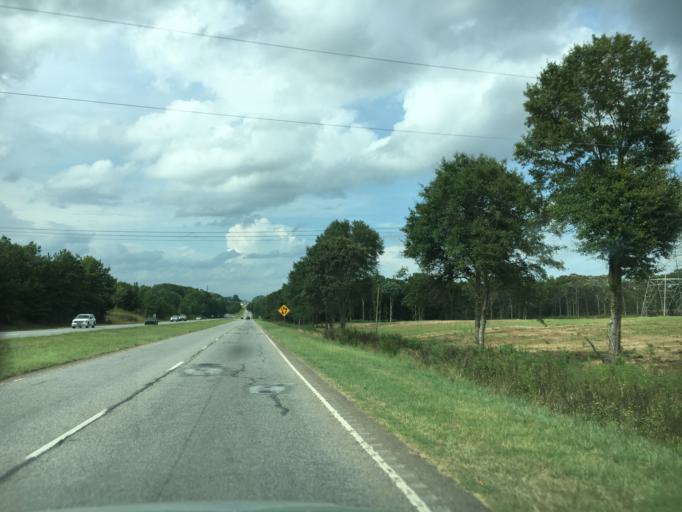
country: US
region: South Carolina
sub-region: Anderson County
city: Piedmont
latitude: 34.6817
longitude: -82.5070
